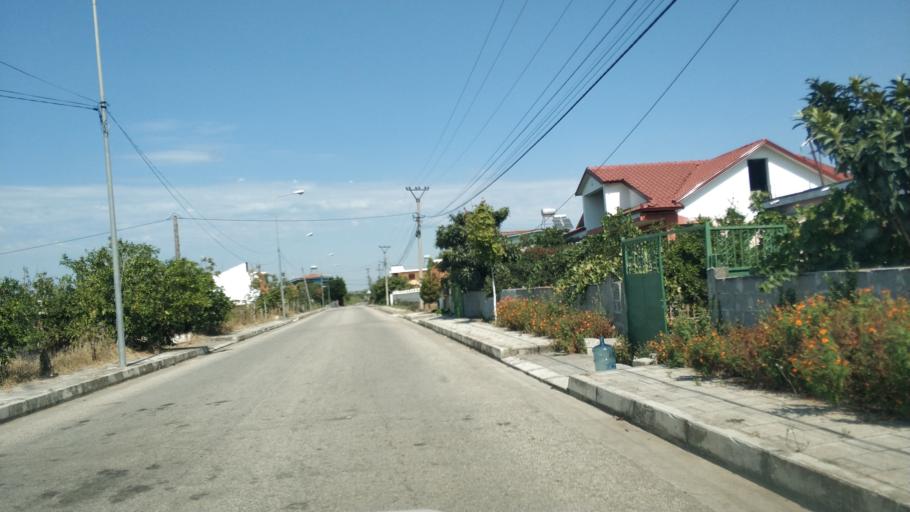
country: AL
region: Fier
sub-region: Rrethi i Lushnjes
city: Divjake
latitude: 41.0012
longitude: 19.5248
